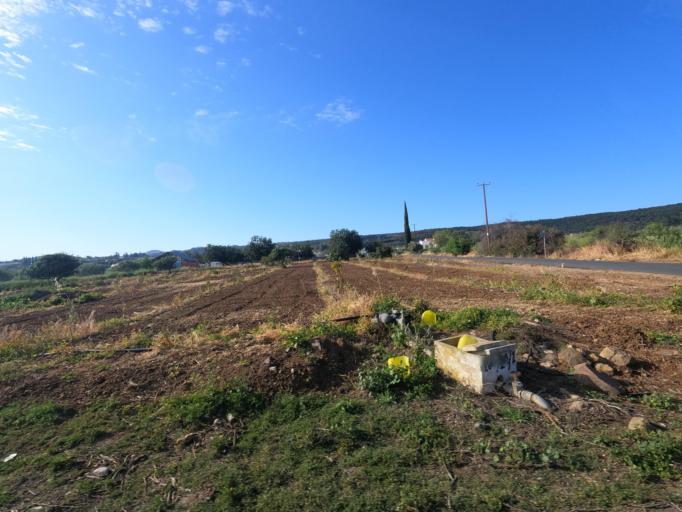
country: CY
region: Pafos
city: Polis
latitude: 35.0330
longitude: 32.3816
